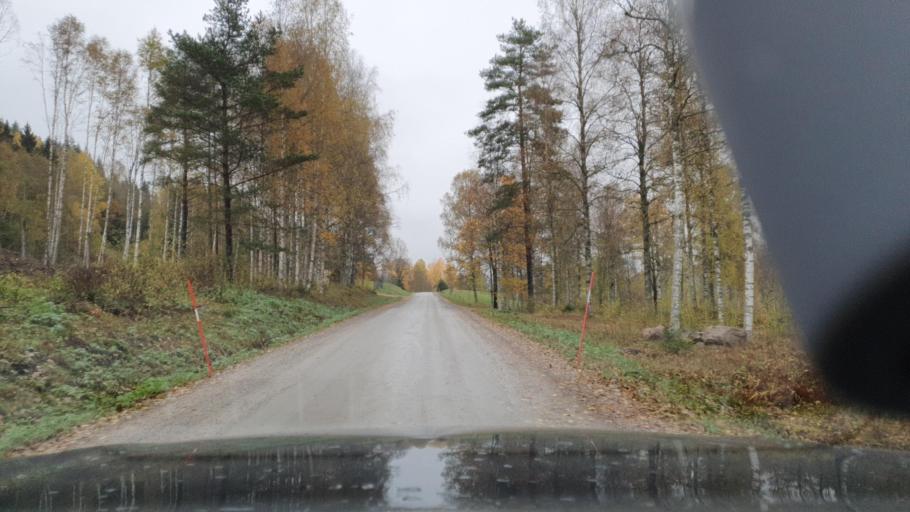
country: SE
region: Vaermland
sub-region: Arvika Kommun
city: Arvika
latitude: 59.8281
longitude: 12.7470
